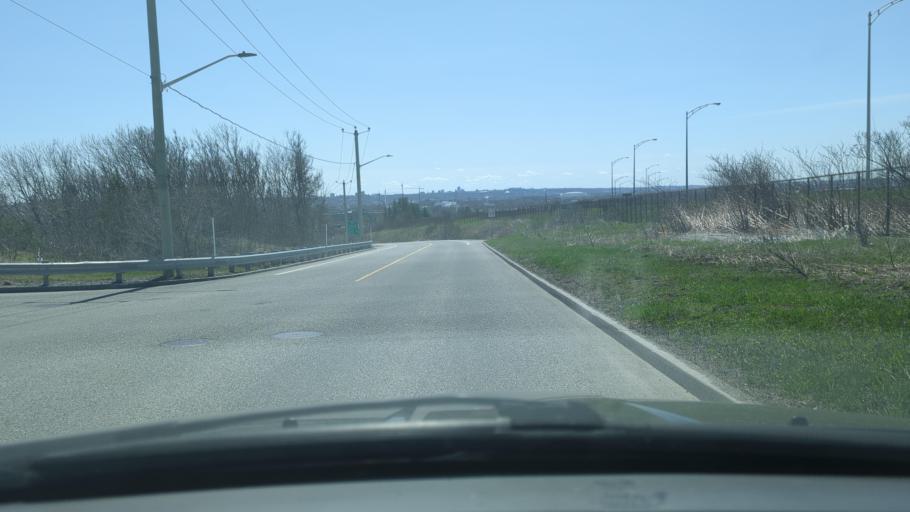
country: CA
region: Quebec
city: Quebec
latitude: 46.8582
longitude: -71.2151
